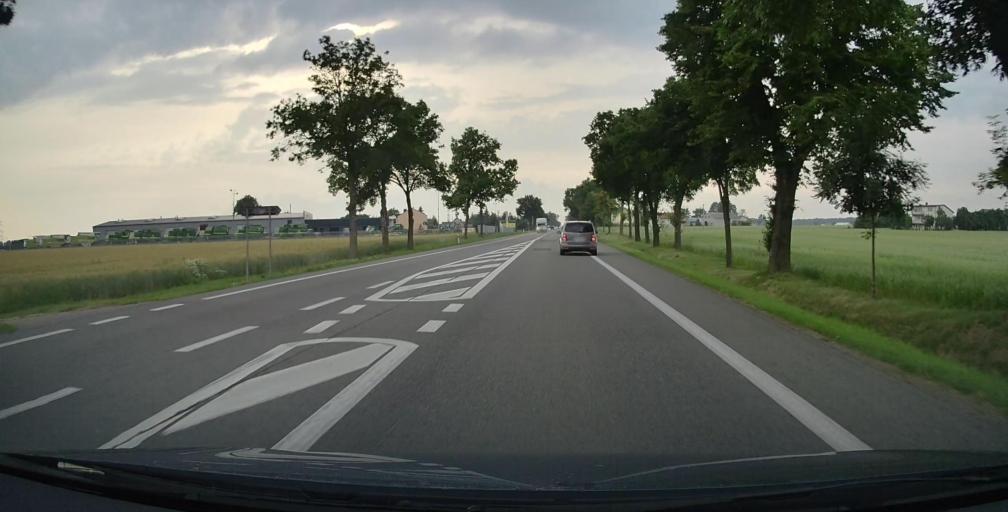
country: PL
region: Masovian Voivodeship
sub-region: Powiat siedlecki
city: Zbuczyn
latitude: 52.1123
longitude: 22.3767
